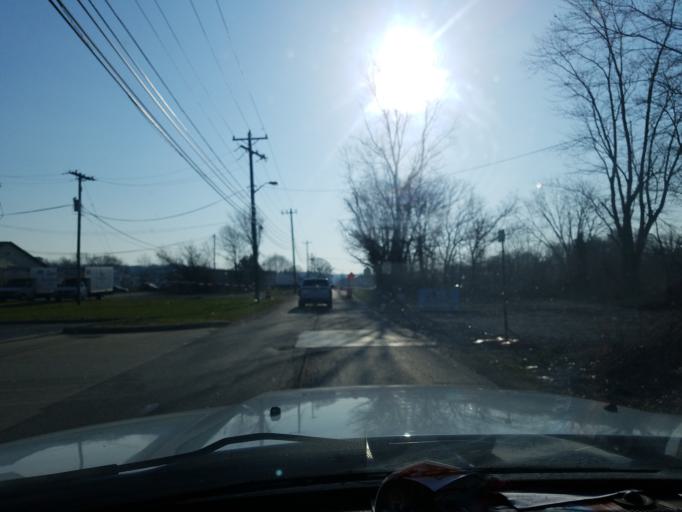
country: US
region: Indiana
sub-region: Owen County
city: Spencer
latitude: 39.2864
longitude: -86.7716
